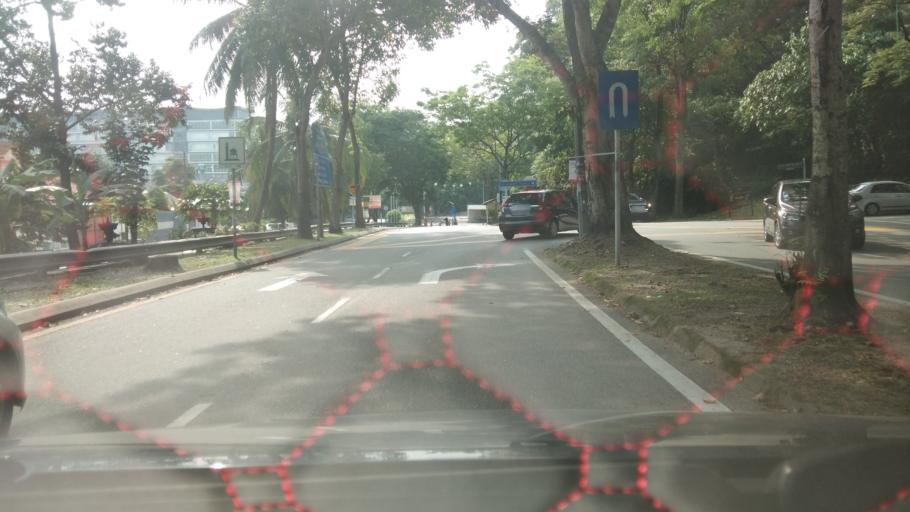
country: MY
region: Selangor
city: Kampong Baharu Balakong
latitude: 3.0739
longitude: 101.7136
